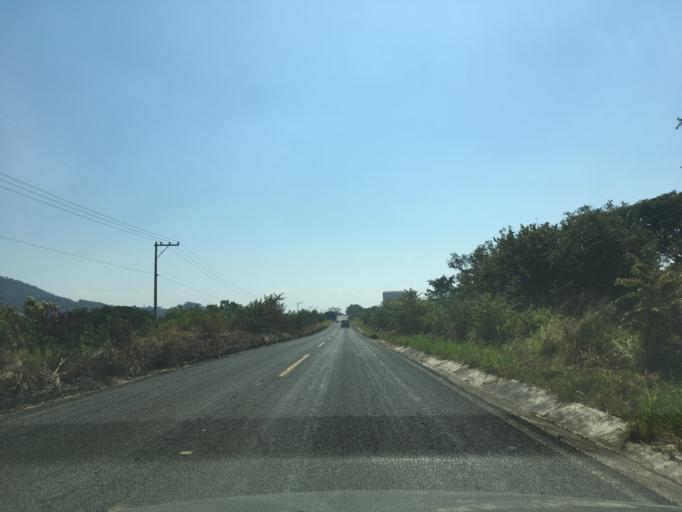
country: MX
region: Michoacan
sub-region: Gabriel Zamora
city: Lombardia
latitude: 19.2463
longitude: -102.0537
